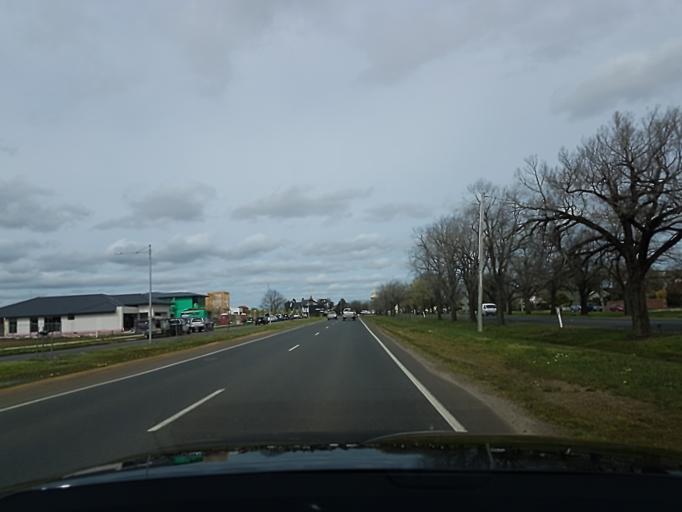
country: AU
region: Victoria
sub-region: Ballarat North
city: Newington
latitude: -37.5517
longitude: 143.8099
